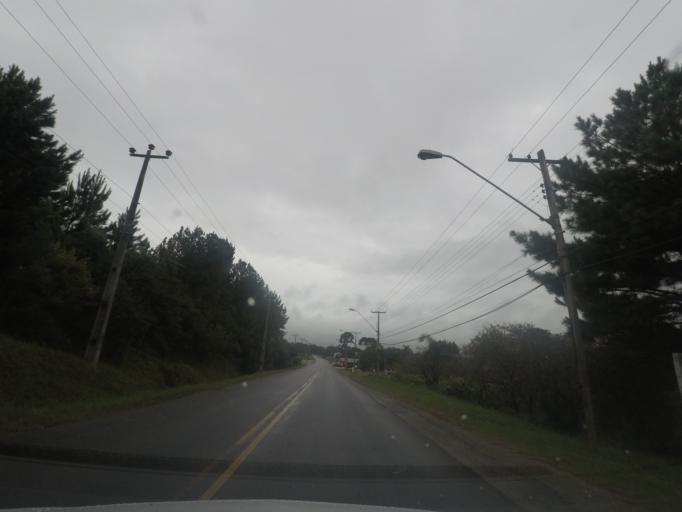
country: BR
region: Parana
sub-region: Campina Grande Do Sul
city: Campina Grande do Sul
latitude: -25.3169
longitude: -49.0748
